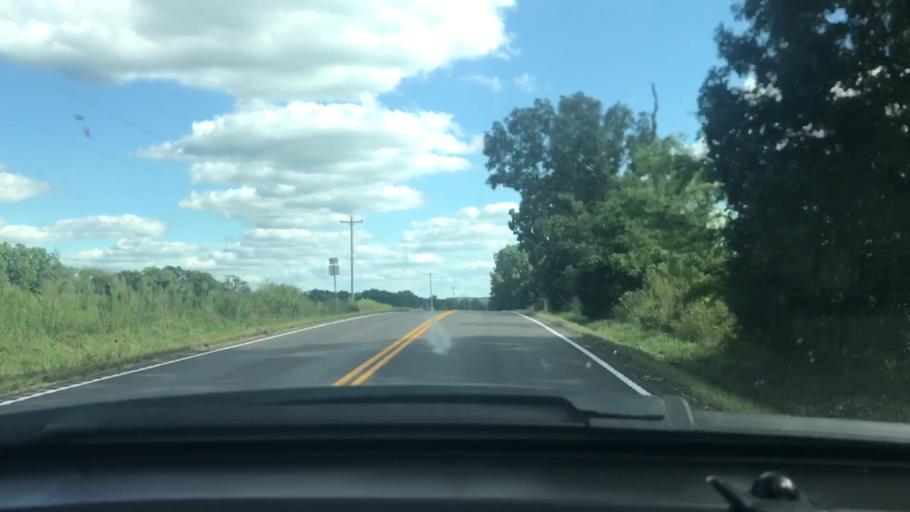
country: US
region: Missouri
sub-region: Wright County
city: Mountain Grove
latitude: 37.2988
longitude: -92.3116
